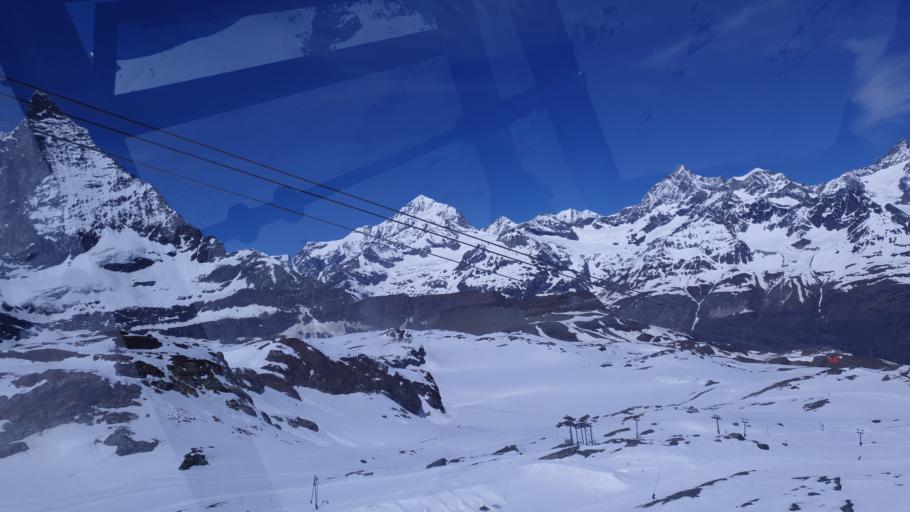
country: CH
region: Valais
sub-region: Visp District
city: Zermatt
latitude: 45.9646
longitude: 7.7230
